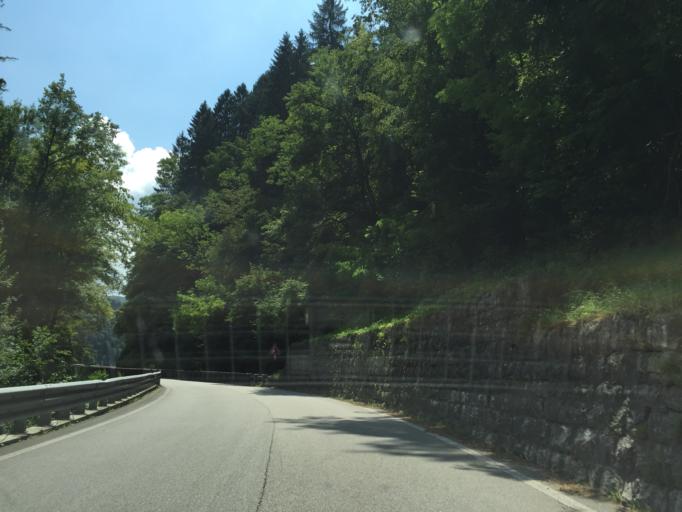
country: IT
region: Veneto
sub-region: Provincia di Belluno
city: Lamon
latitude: 46.0570
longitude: 11.7626
